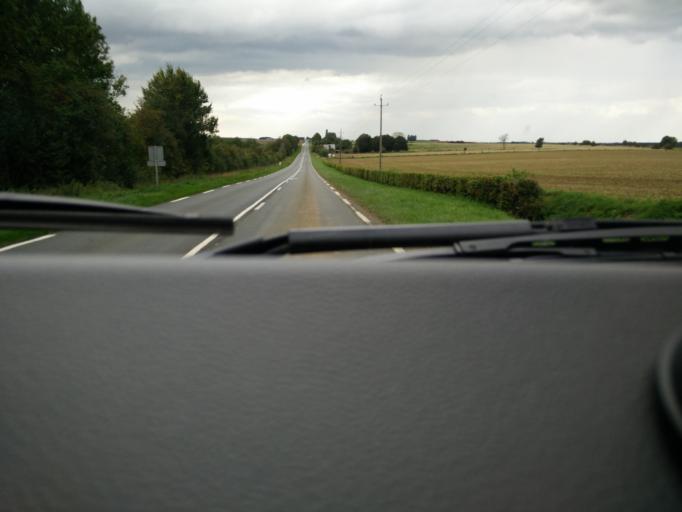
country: FR
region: Champagne-Ardenne
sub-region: Departement des Ardennes
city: Signy-le-Petit
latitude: 49.8646
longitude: 4.2304
